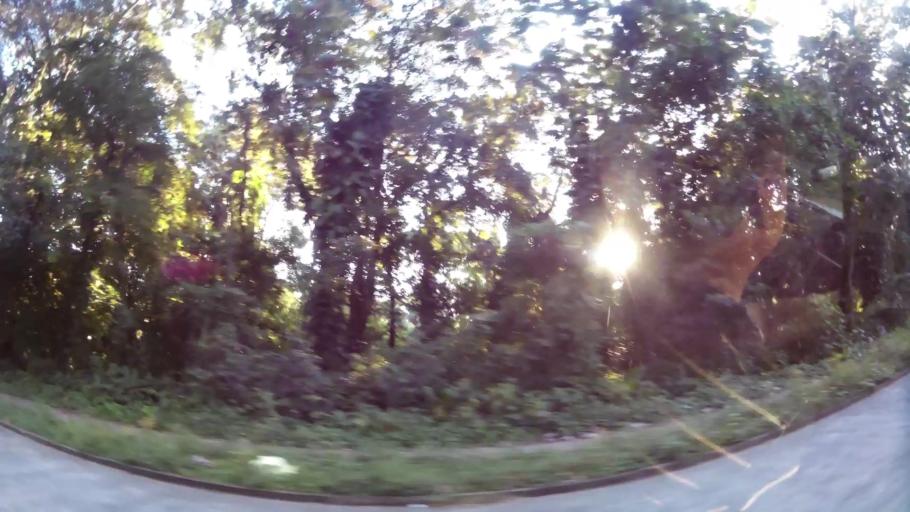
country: GT
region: Suchitepeque
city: Mazatenango
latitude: 14.5421
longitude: -91.5056
